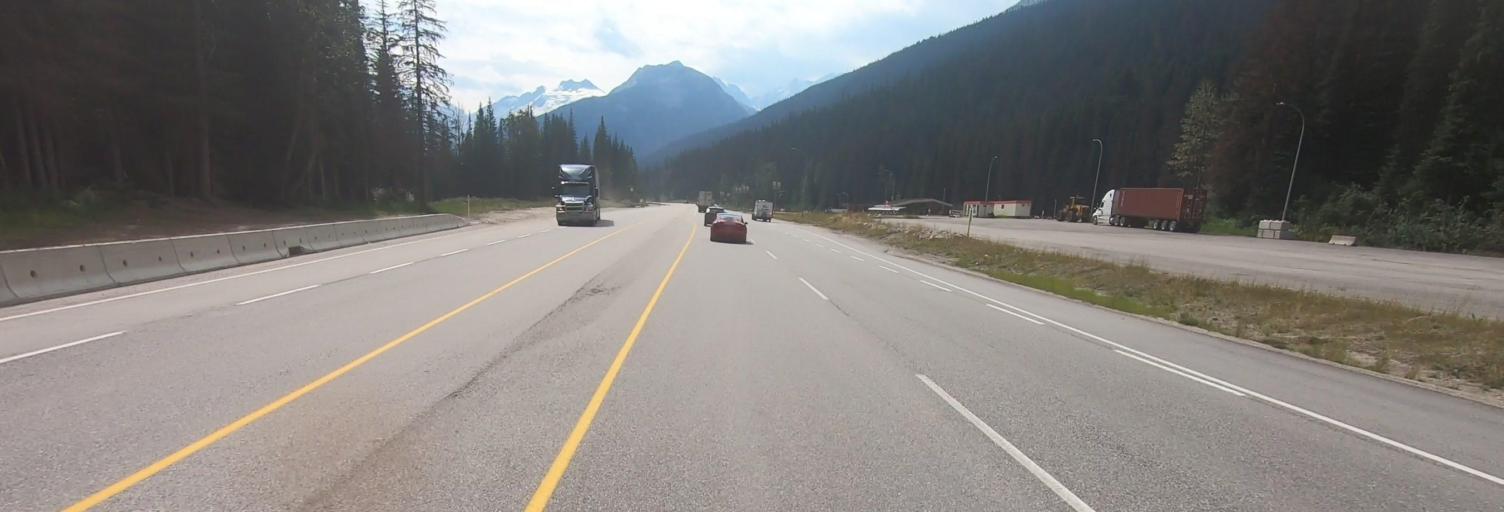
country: CA
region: British Columbia
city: Golden
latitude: 51.3036
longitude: -117.5202
